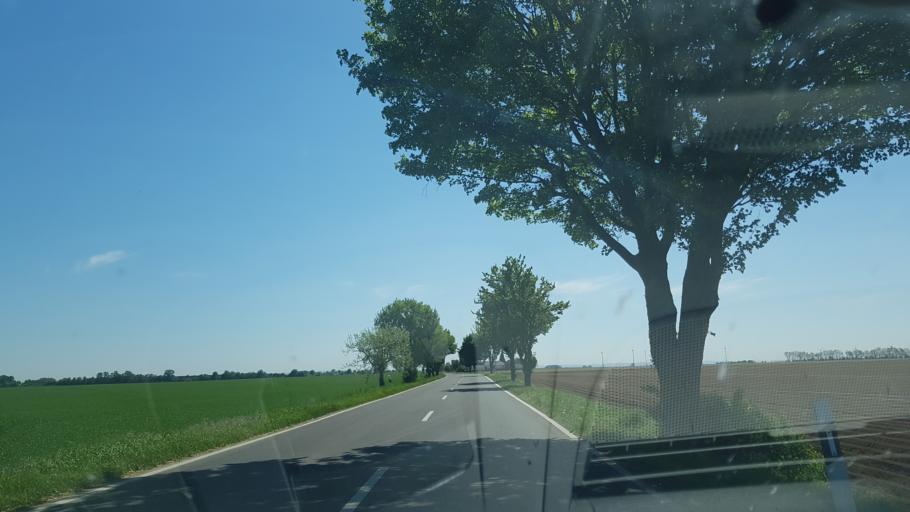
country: DE
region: North Rhine-Westphalia
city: Tuernich
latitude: 50.8187
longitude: 6.7213
